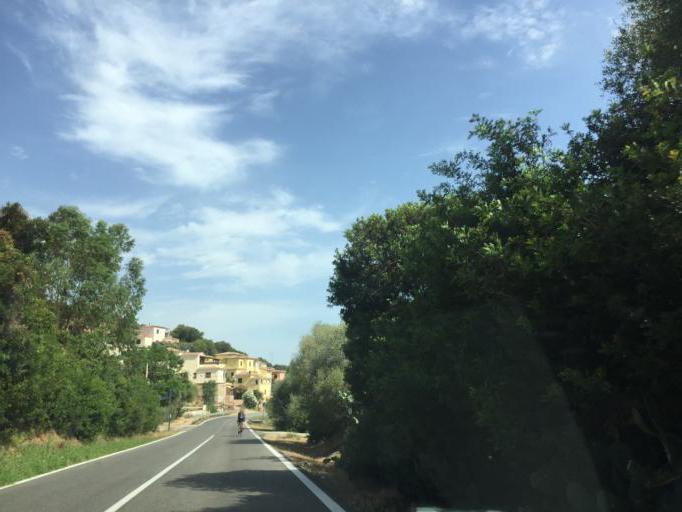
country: IT
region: Sardinia
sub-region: Provincia di Olbia-Tempio
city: San Teodoro
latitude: 40.7390
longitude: 9.6465
